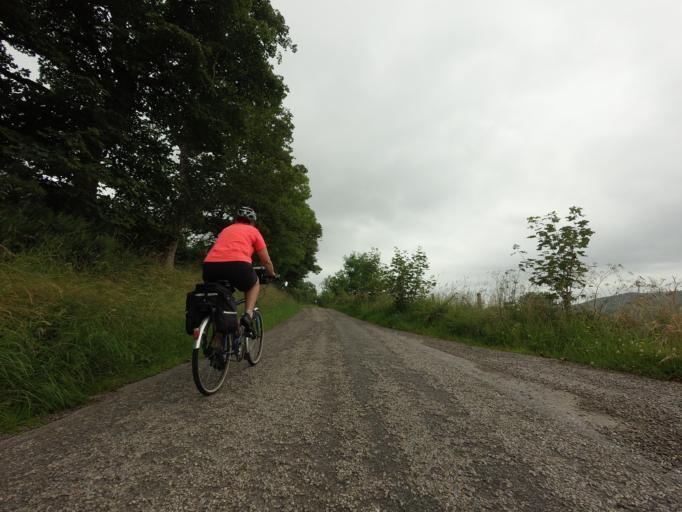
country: GB
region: Scotland
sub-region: Highland
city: Alness
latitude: 57.8979
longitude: -4.3782
